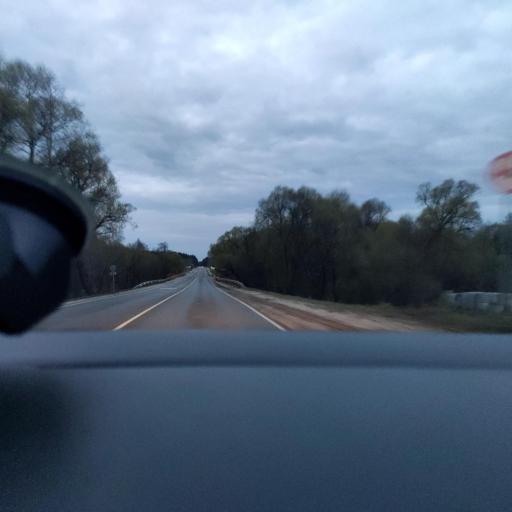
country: RU
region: Moskovskaya
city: Krasnyy Tkach
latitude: 55.4253
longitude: 39.1913
